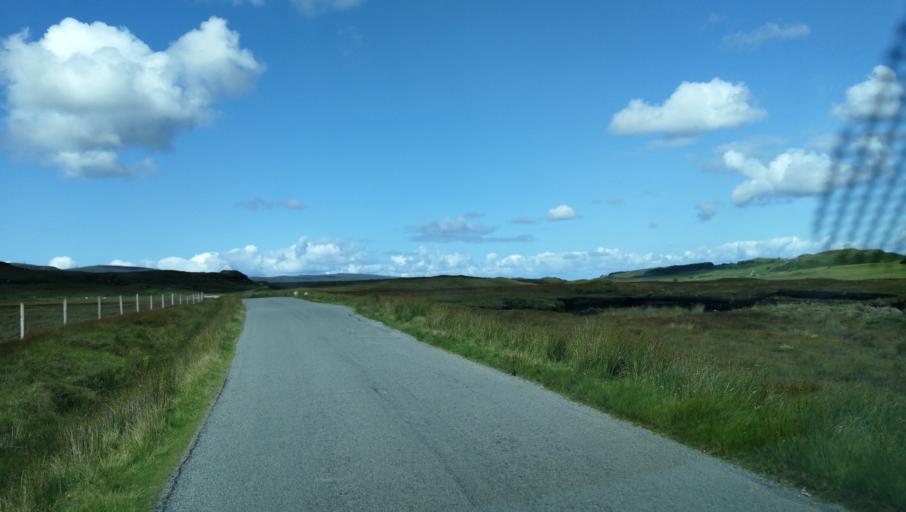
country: GB
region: Scotland
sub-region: Highland
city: Isle of Skye
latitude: 57.4210
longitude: -6.5870
